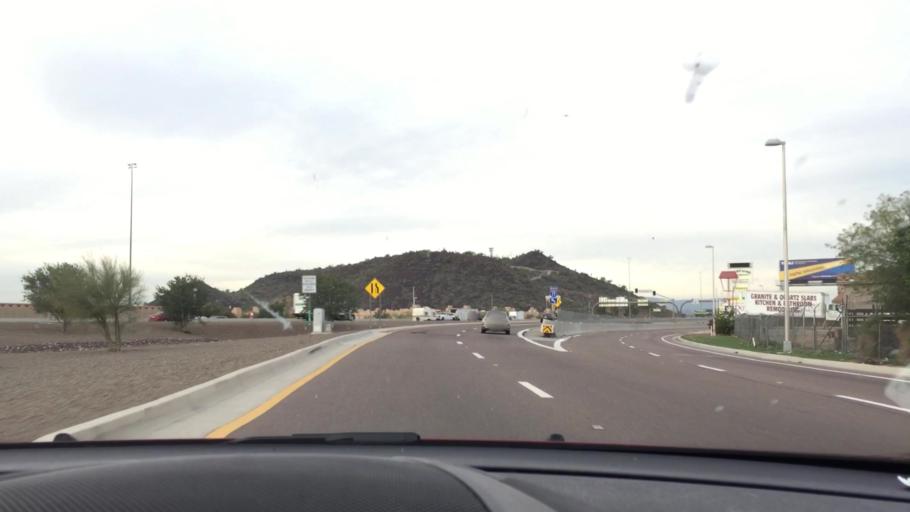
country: US
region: Arizona
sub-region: Maricopa County
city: Peoria
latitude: 33.6852
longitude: -112.1114
